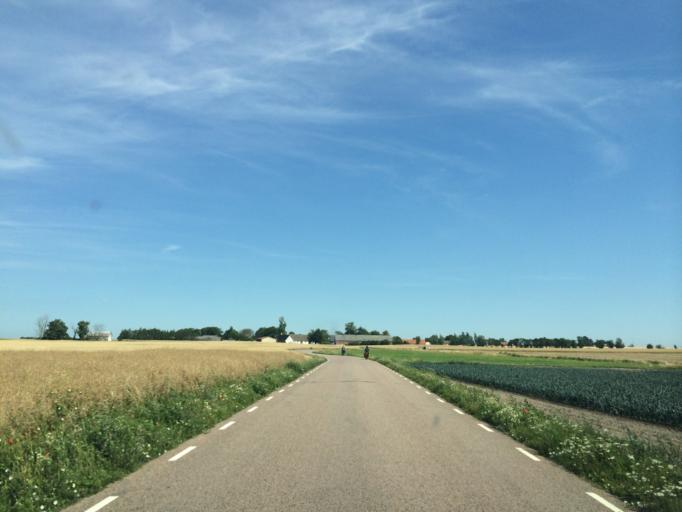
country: SE
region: Skane
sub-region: Trelleborgs Kommun
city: Skare
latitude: 55.4170
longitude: 13.0833
